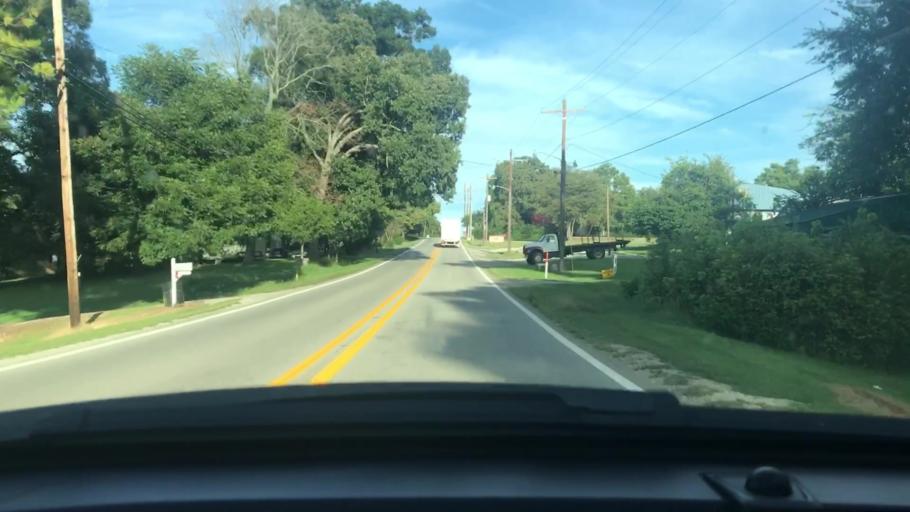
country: US
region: Arkansas
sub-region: Randolph County
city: Pocahontas
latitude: 36.2039
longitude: -91.1885
